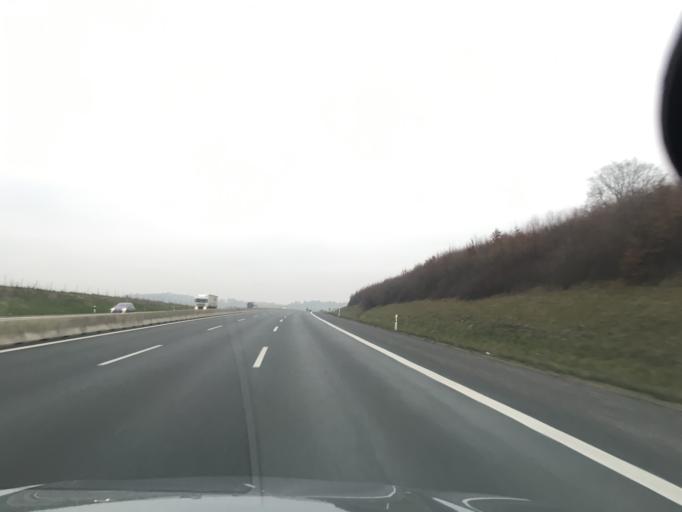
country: DE
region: Bavaria
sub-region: Regierungsbezirk Unterfranken
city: Uettingen
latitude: 49.7726
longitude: 9.7430
